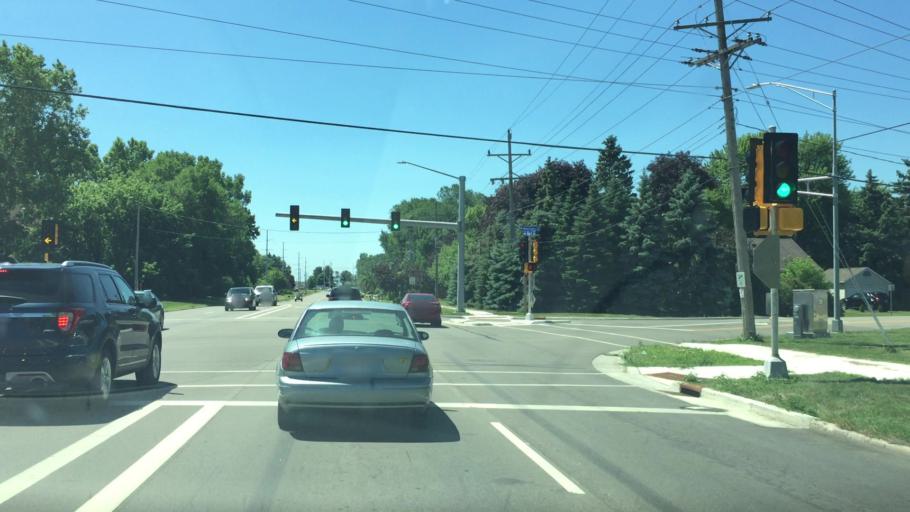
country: US
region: Wisconsin
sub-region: Outagamie County
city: Appleton
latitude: 44.2187
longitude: -88.4043
